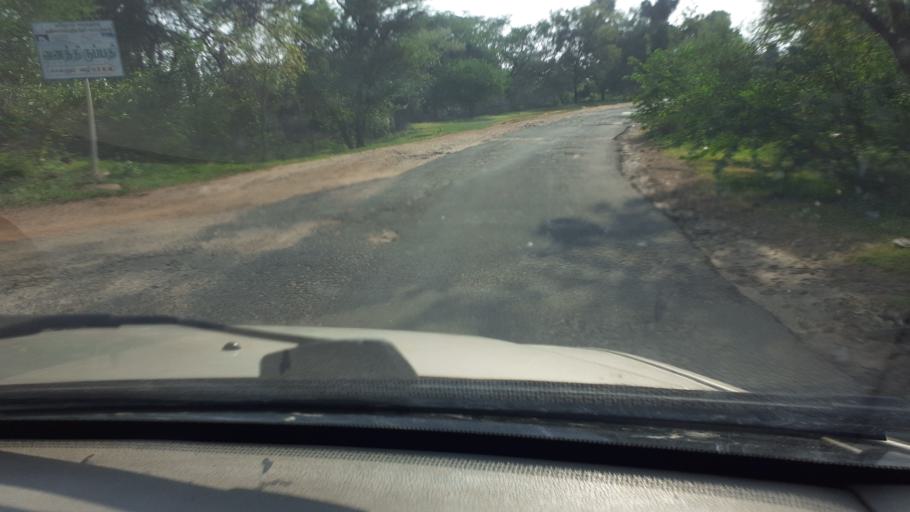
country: IN
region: Tamil Nadu
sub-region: Thoothukkudi
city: Eral
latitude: 8.5735
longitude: 78.0218
